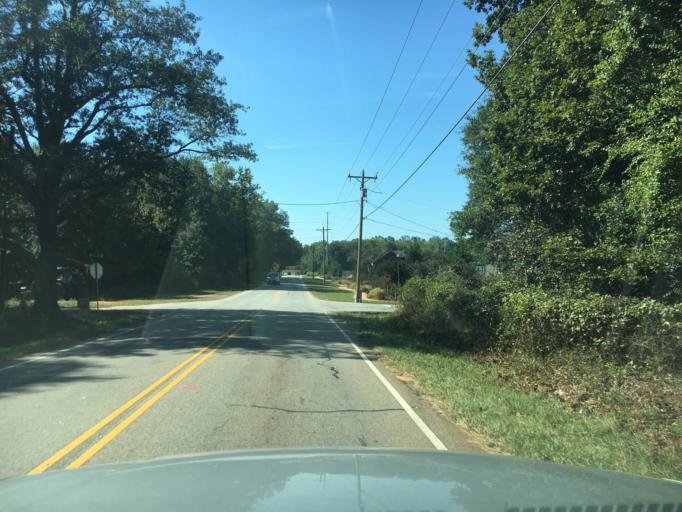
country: US
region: South Carolina
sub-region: Greenville County
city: Taylors
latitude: 34.9122
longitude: -82.2709
